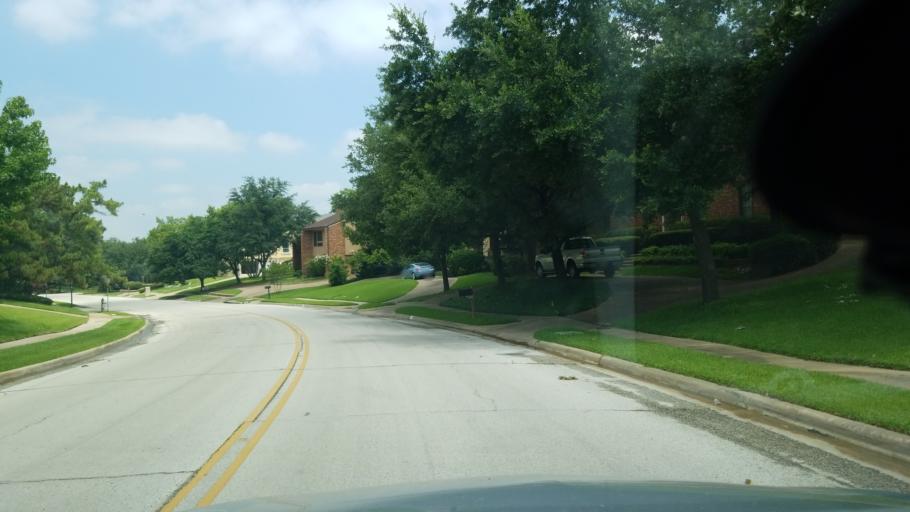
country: US
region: Texas
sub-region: Dallas County
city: Irving
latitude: 32.8542
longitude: -96.9416
